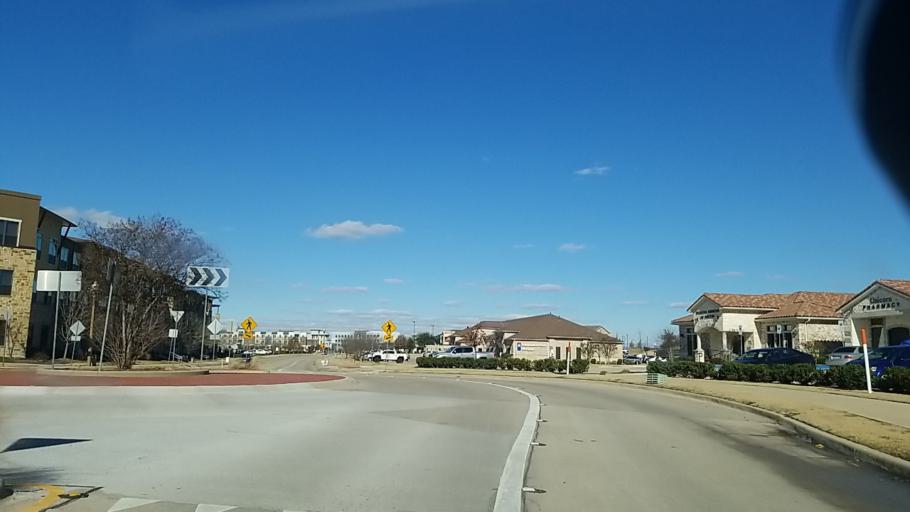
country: US
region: Texas
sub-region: Denton County
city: Corinth
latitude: 33.1730
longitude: -97.0963
